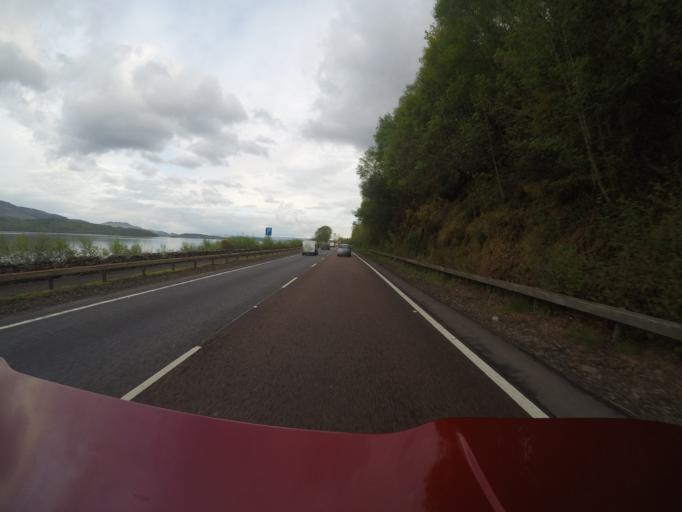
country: GB
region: Scotland
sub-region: Argyll and Bute
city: Helensburgh
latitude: 56.1344
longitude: -4.6578
